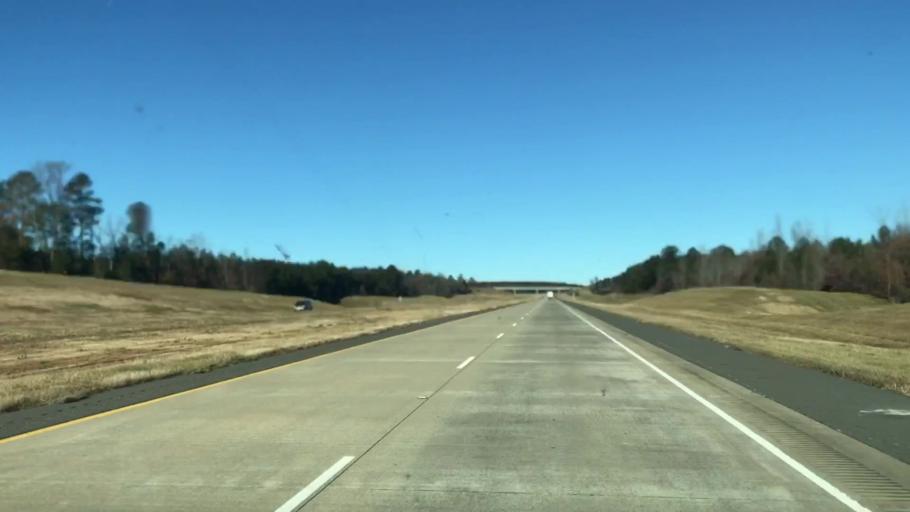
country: US
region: Louisiana
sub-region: Caddo Parish
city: Vivian
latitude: 32.9152
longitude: -93.8767
